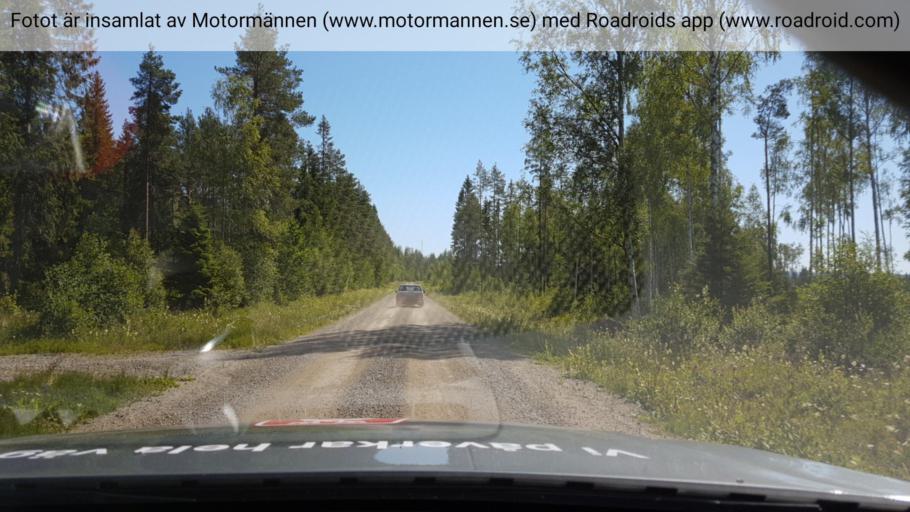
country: SE
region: Jaemtland
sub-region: Braecke Kommun
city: Braecke
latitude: 62.7978
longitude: 15.2562
